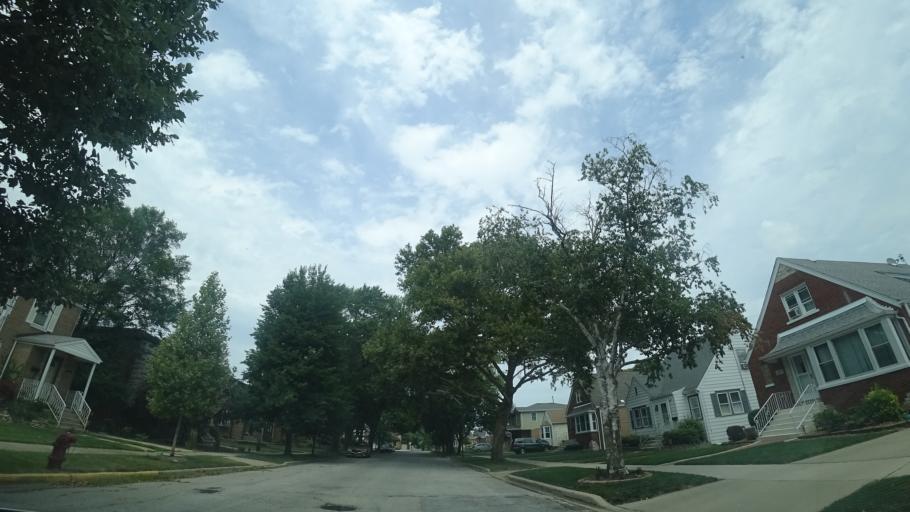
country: US
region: Illinois
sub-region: Cook County
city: Merrionette Park
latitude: 41.6976
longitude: -87.7145
